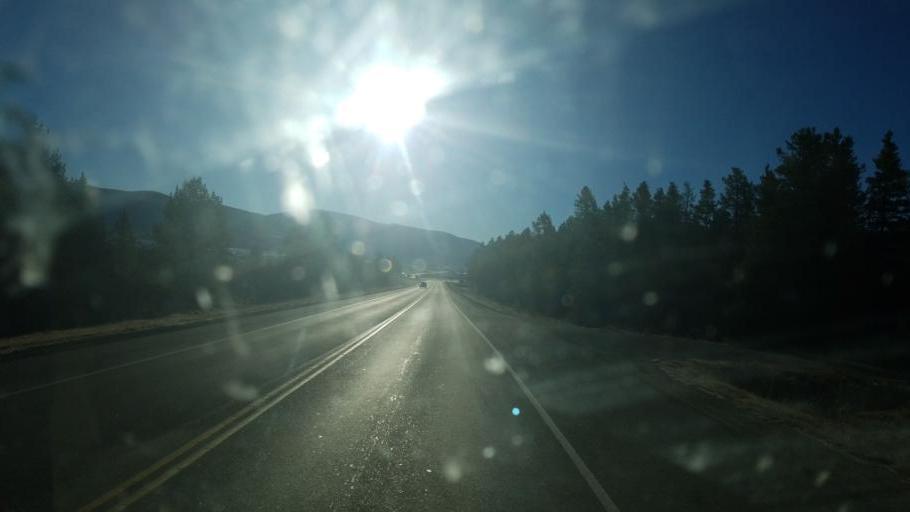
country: US
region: Colorado
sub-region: Gunnison County
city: Crested Butte
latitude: 38.8615
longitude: -106.9730
